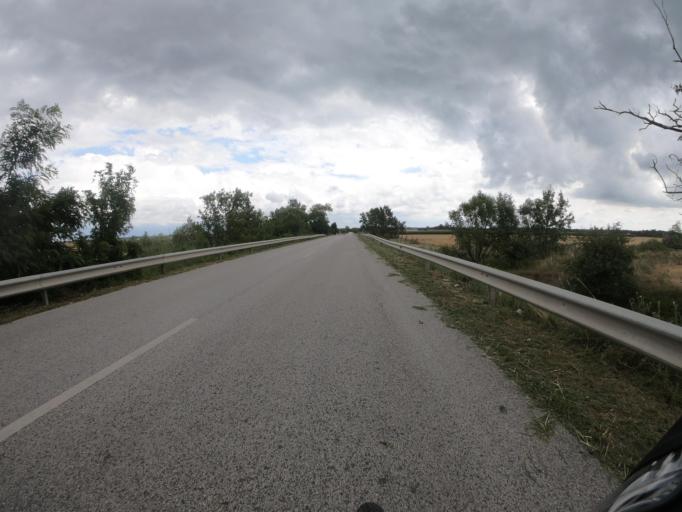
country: HU
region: Heves
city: Poroszlo
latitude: 47.6939
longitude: 20.7330
